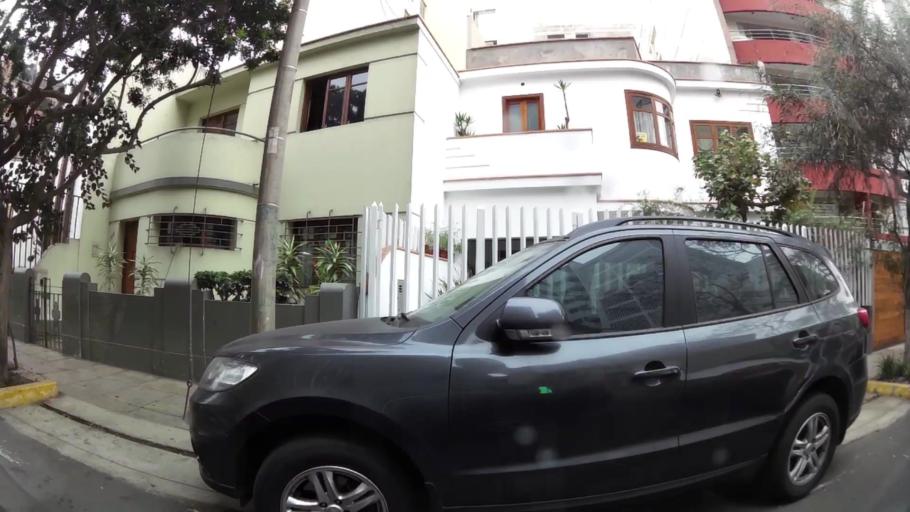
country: PE
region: Lima
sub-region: Lima
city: Surco
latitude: -12.1277
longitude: -77.0259
